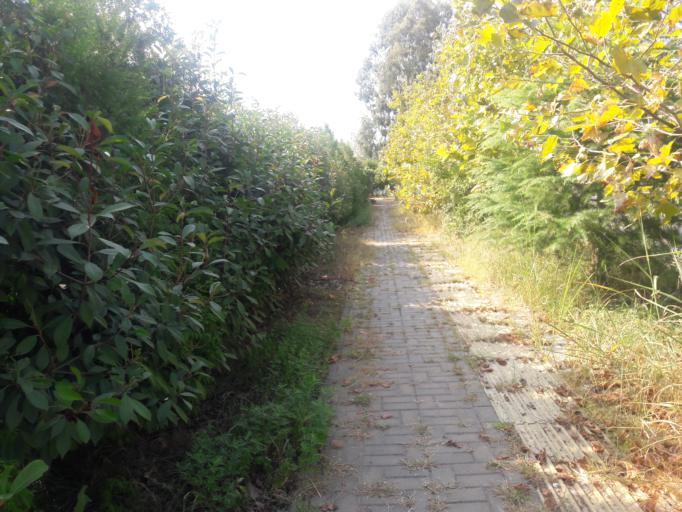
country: RU
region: Krasnodarskiy
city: Vysokoye
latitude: 43.3940
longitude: 39.9983
